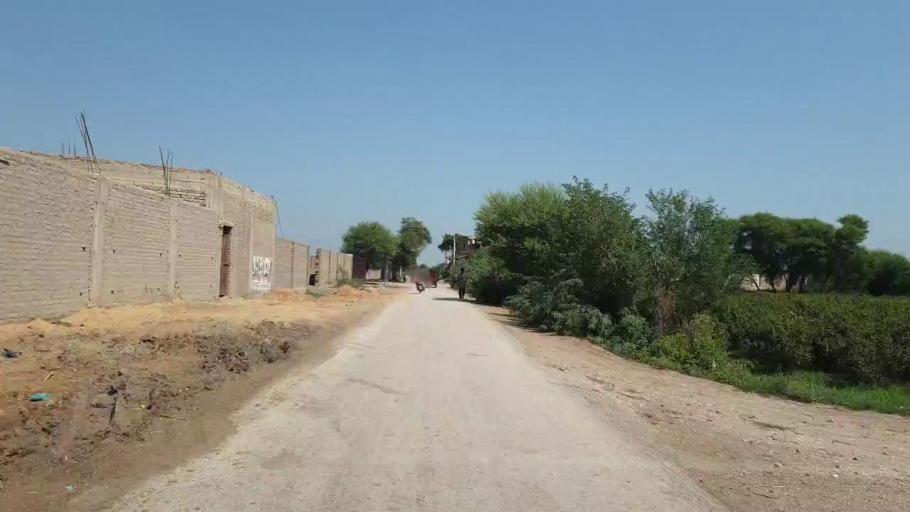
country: PK
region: Sindh
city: Hyderabad
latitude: 25.4506
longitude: 68.4159
